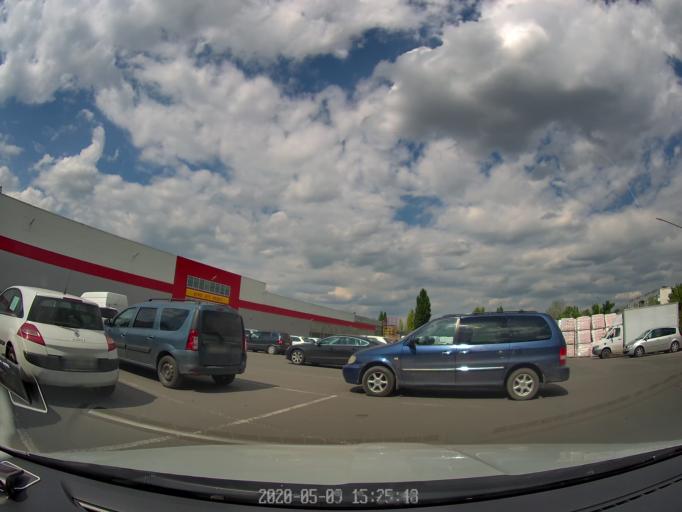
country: MD
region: Chisinau
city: Chisinau
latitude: 46.9787
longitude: 28.8794
